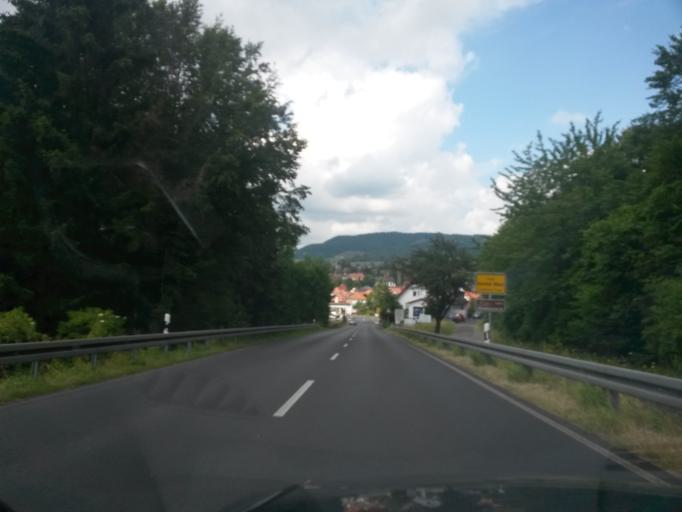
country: DE
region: Hesse
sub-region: Regierungsbezirk Kassel
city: Gersfeld
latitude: 50.4462
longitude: 9.9202
